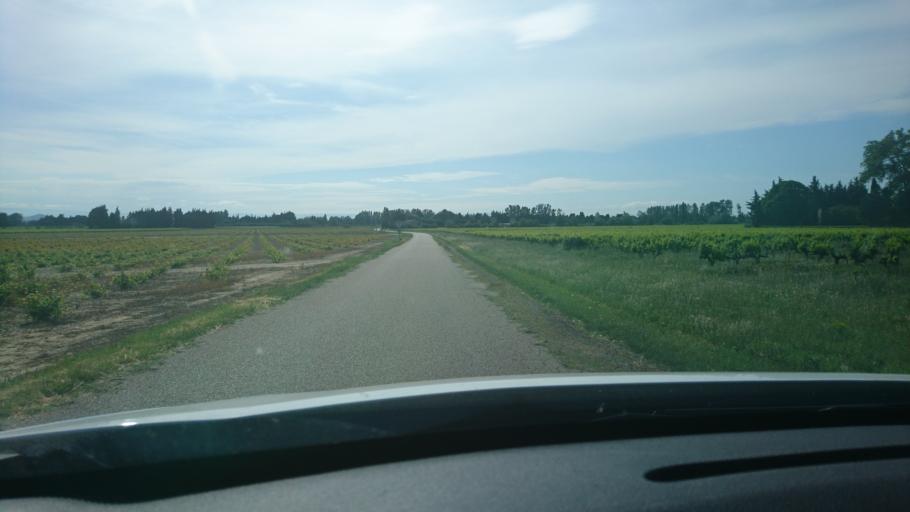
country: FR
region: Provence-Alpes-Cote d'Azur
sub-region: Departement du Vaucluse
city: Jonquieres
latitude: 44.1346
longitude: 4.8796
